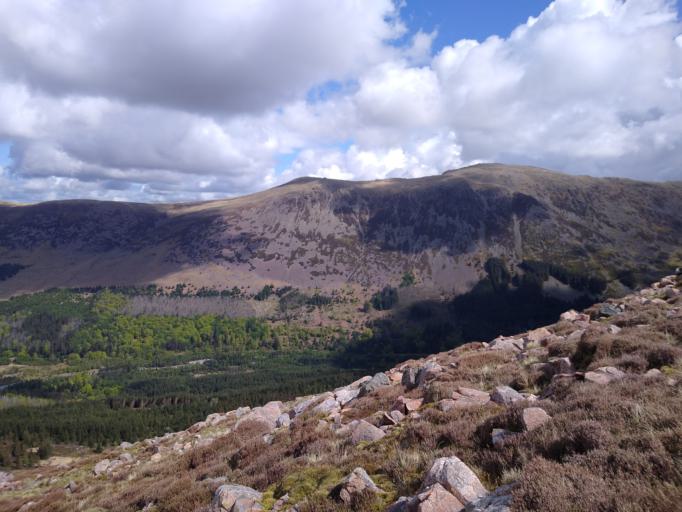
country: GB
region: England
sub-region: Cumbria
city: Cockermouth
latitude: 54.5011
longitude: -3.3103
